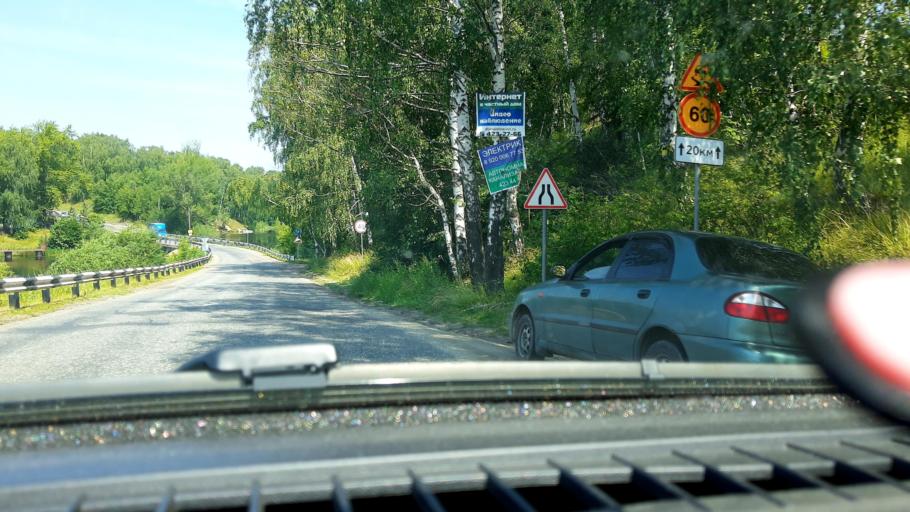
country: RU
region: Nizjnij Novgorod
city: Gorodets
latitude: 56.6867
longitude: 43.4301
